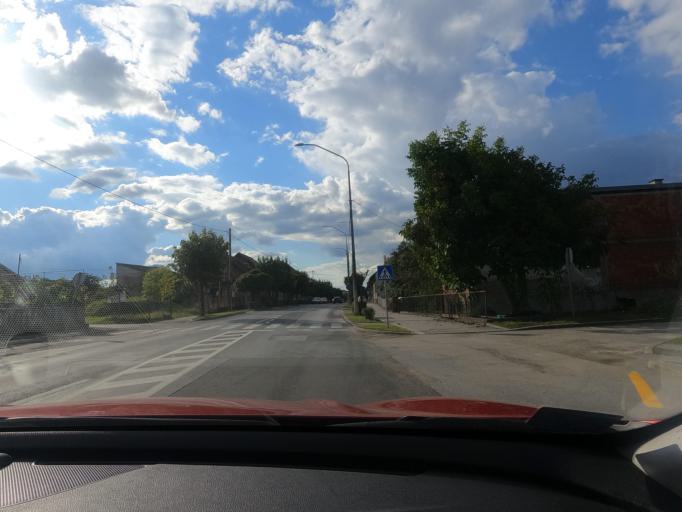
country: HR
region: Sisacko-Moslavacka
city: Petrinja
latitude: 45.4430
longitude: 16.2891
